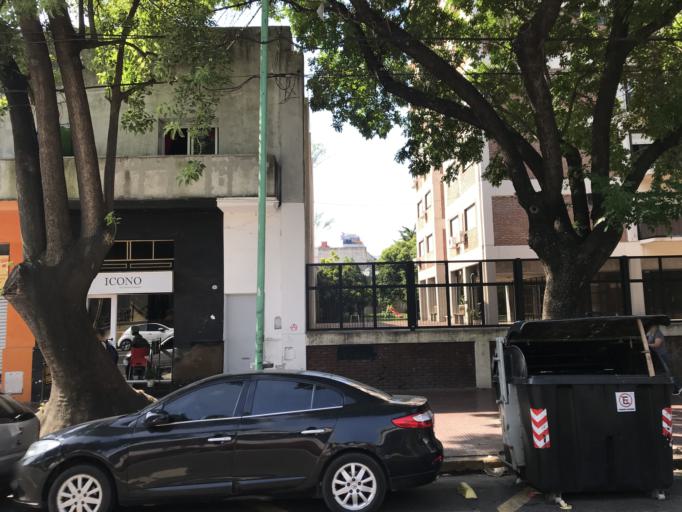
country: AR
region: Buenos Aires F.D.
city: Buenos Aires
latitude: -34.6386
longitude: -58.4139
